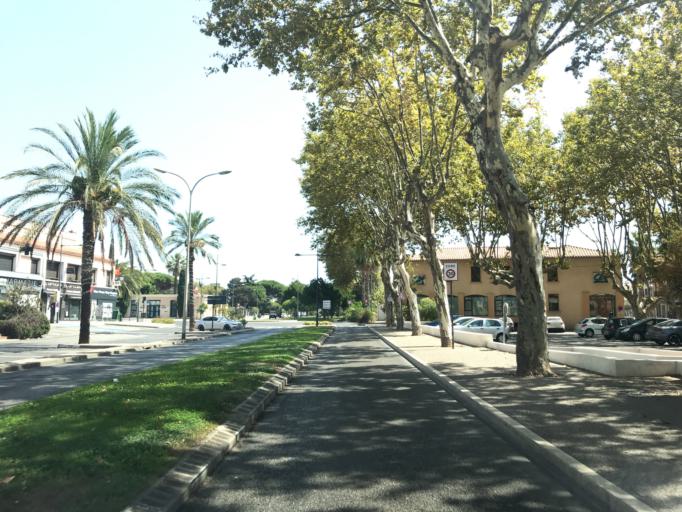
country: FR
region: Provence-Alpes-Cote d'Azur
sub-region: Departement du Var
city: Six-Fours-les-Plages
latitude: 43.0941
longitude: 5.8369
